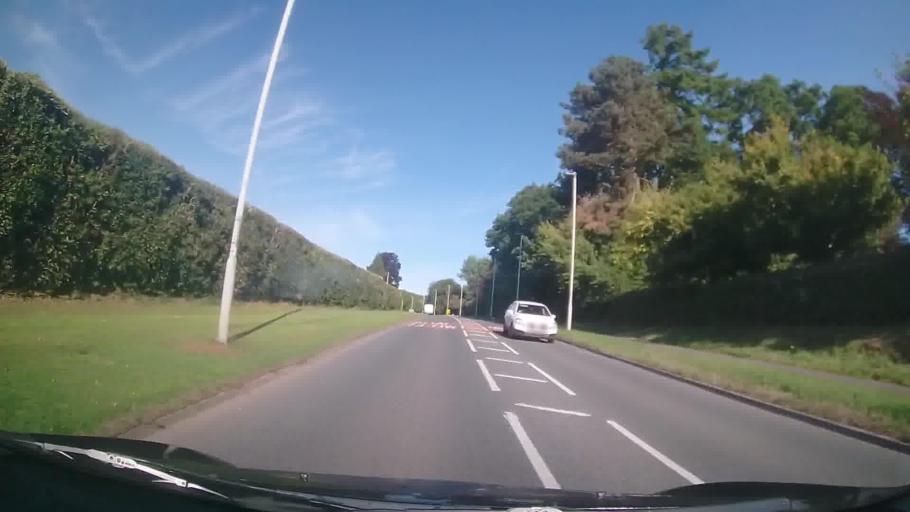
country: GB
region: Wales
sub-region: Sir Powys
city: Hay
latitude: 52.0029
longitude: -3.2410
